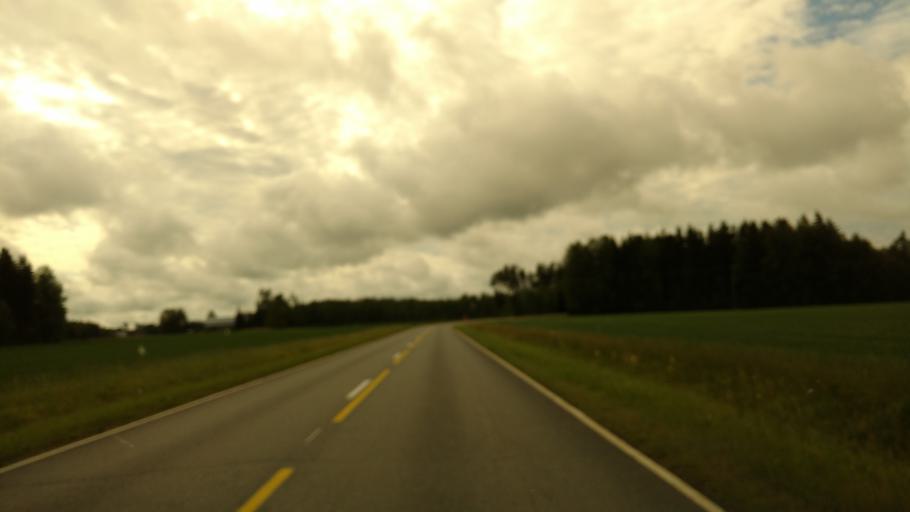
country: FI
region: Varsinais-Suomi
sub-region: Loimaa
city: Koski Tl
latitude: 60.5892
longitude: 23.1330
